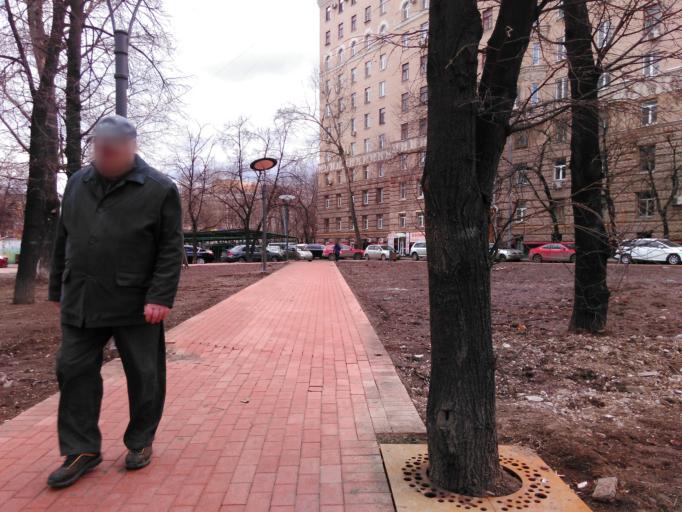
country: RU
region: Moscow
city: Mar'ina Roshcha
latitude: 55.8049
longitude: 37.6374
